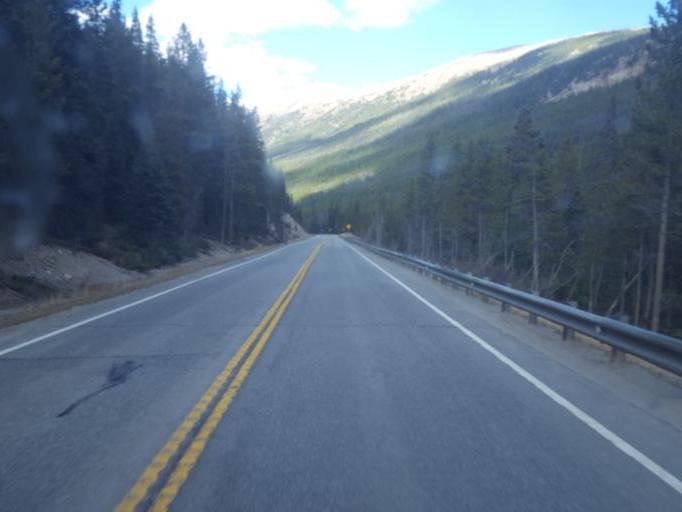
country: US
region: Colorado
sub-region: Summit County
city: Breckenridge
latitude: 39.4699
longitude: -106.1326
